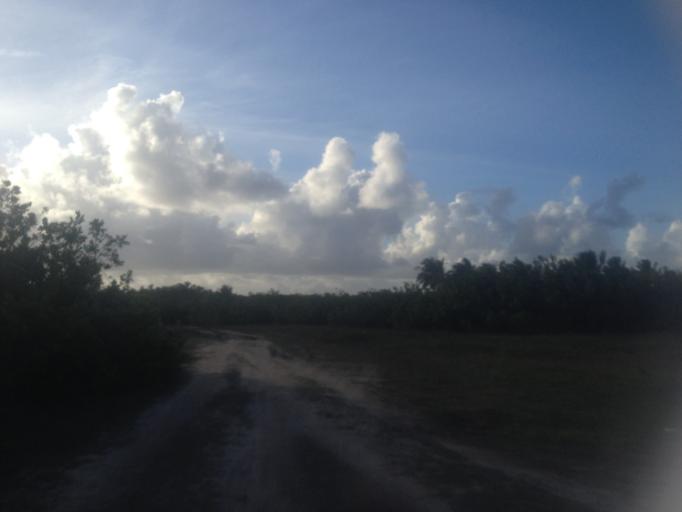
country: BR
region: Sergipe
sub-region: Indiaroba
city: Indiaroba
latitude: -11.4656
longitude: -37.3575
